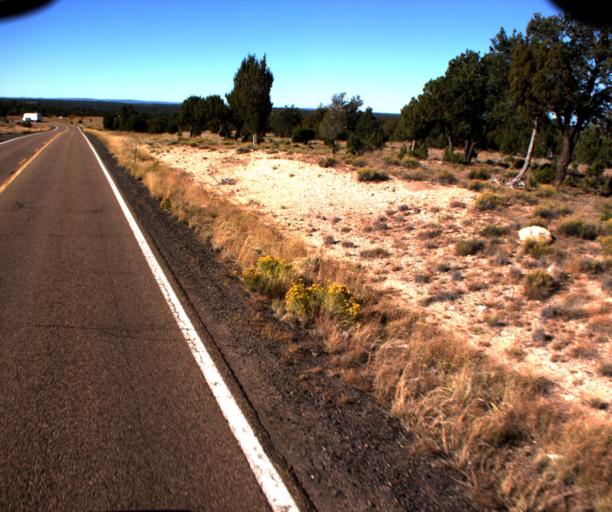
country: US
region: Arizona
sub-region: Navajo County
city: Heber-Overgaard
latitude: 34.4670
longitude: -110.4746
